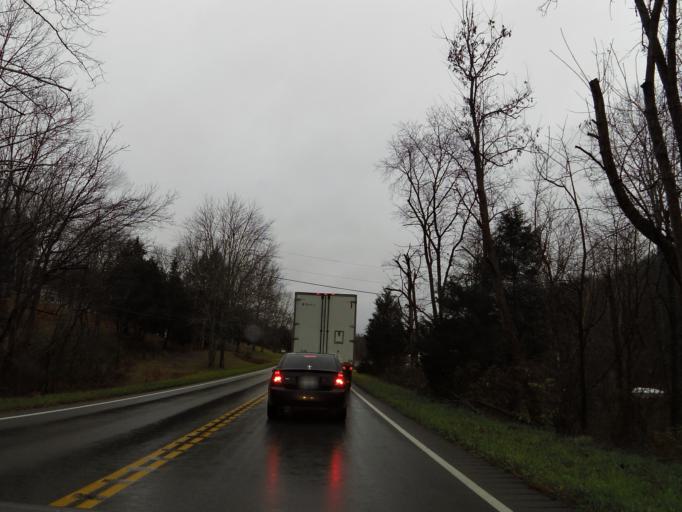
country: US
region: Kentucky
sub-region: Rockcastle County
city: Mount Vernon
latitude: 37.3981
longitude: -84.3343
